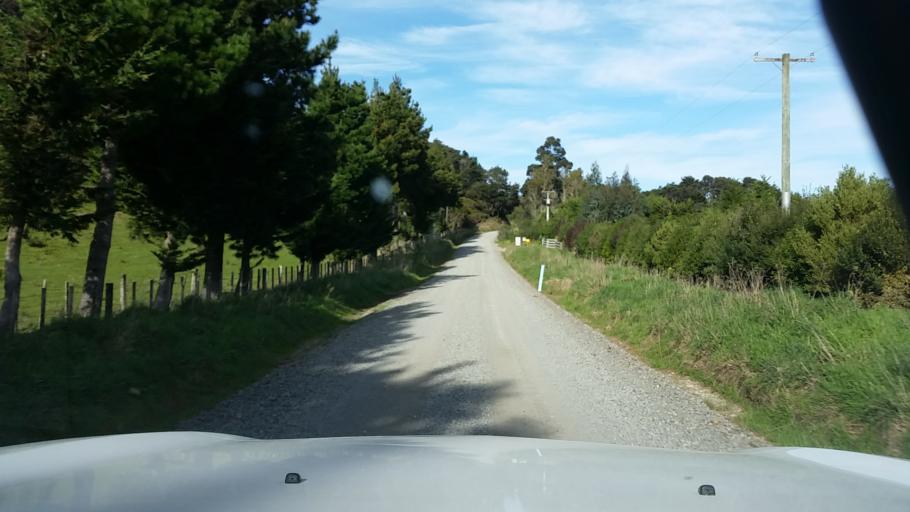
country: NZ
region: Wellington
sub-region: Masterton District
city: Masterton
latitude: -41.0376
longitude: 175.4015
